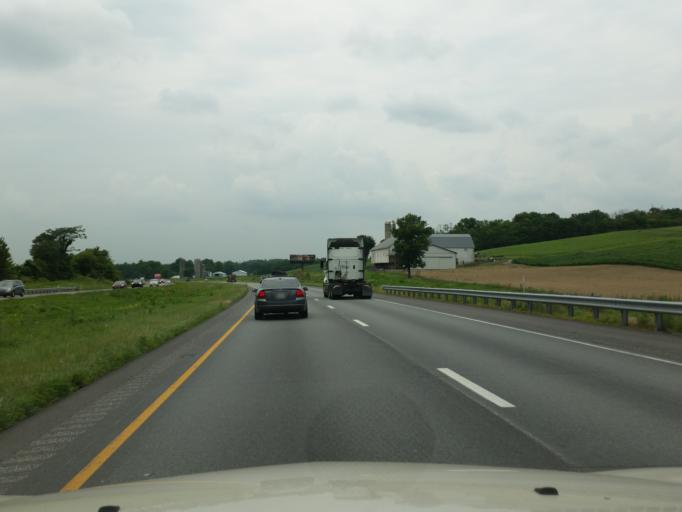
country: US
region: Pennsylvania
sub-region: Lancaster County
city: Mount Joy
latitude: 40.1301
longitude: -76.4815
